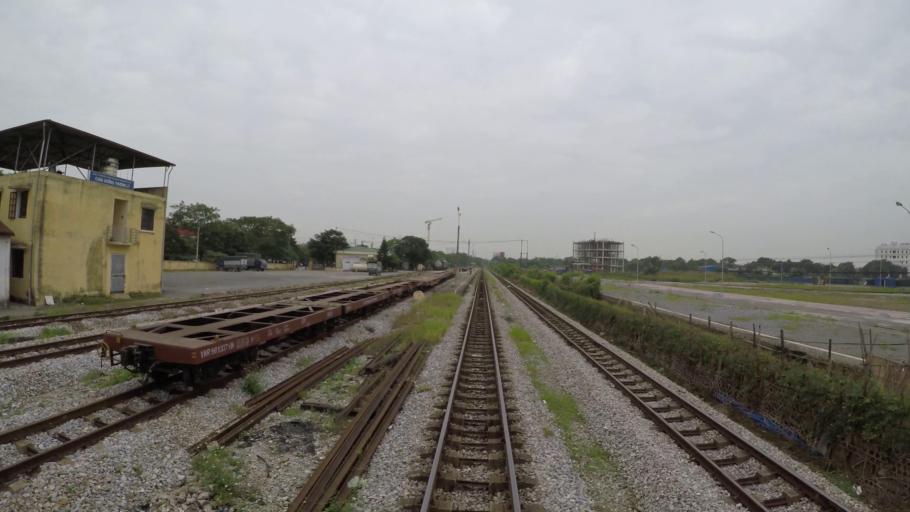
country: VN
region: Hai Phong
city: An Duong
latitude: 20.8837
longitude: 106.6092
